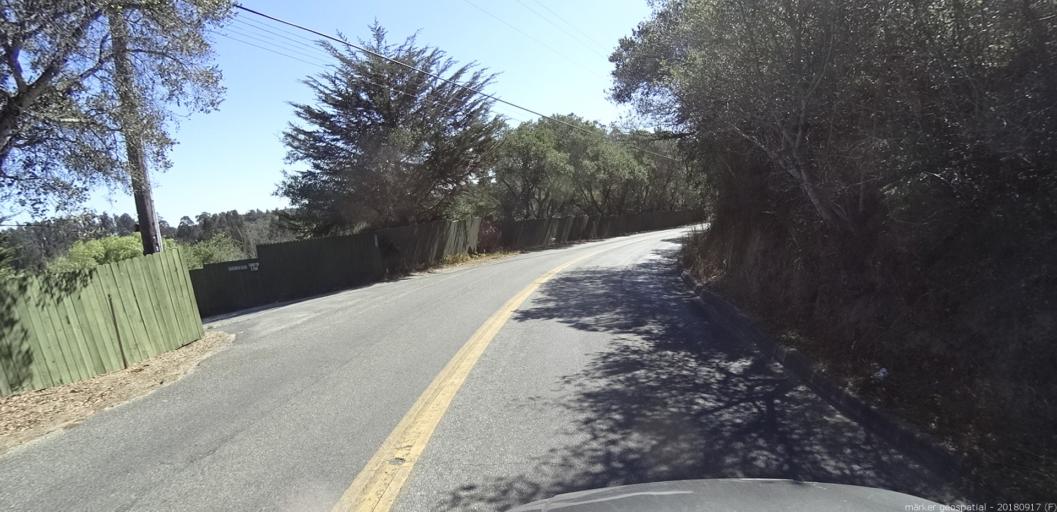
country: US
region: California
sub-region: Monterey County
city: Prunedale
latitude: 36.8326
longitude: -121.6827
